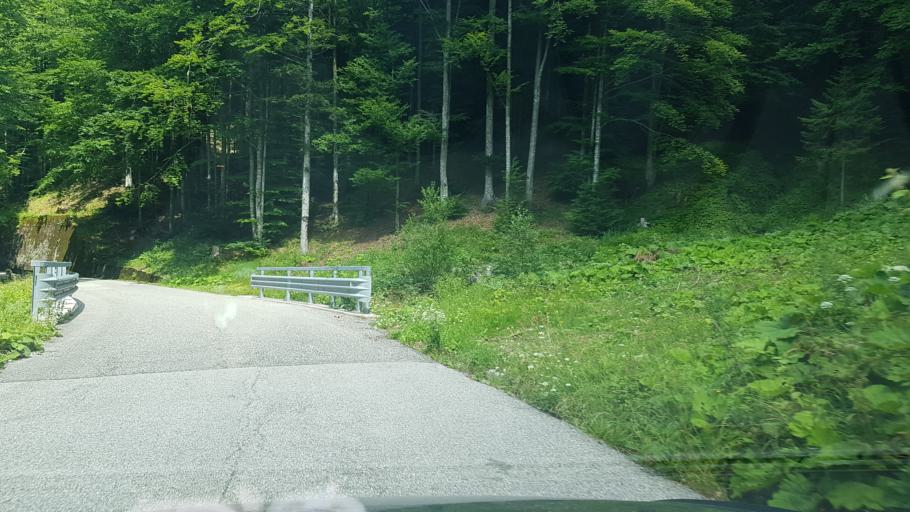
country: IT
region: Friuli Venezia Giulia
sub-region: Provincia di Udine
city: Pontebba
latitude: 46.5026
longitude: 13.2425
